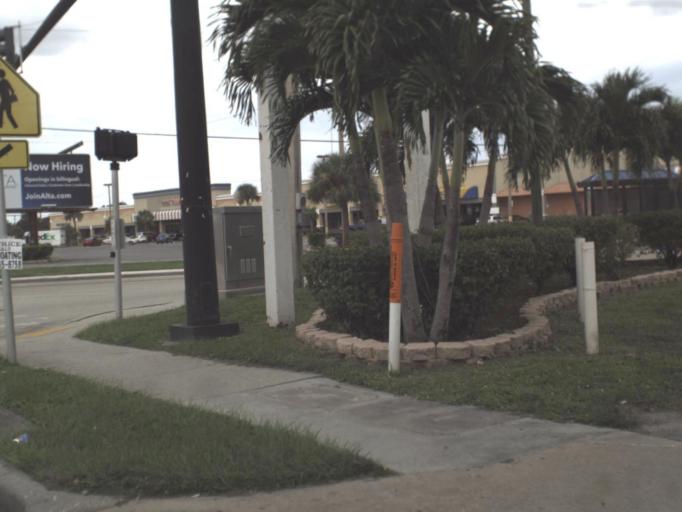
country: US
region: Florida
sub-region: Lee County
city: Tice
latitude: 26.6676
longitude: -81.8283
